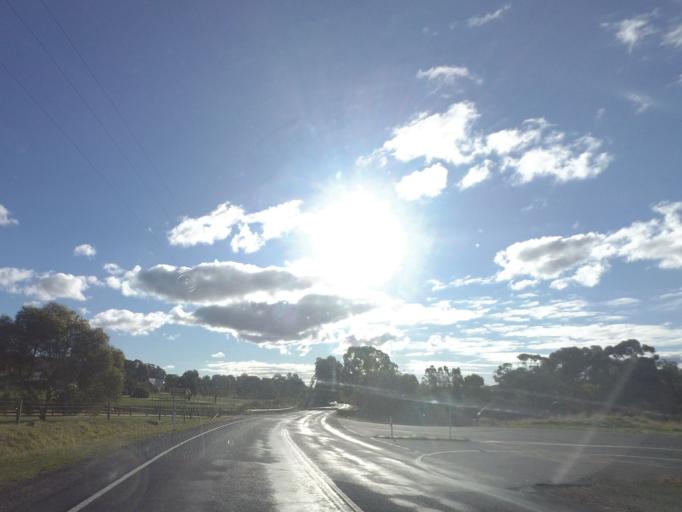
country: AU
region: Victoria
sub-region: Mount Alexander
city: Castlemaine
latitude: -37.0954
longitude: 144.2897
